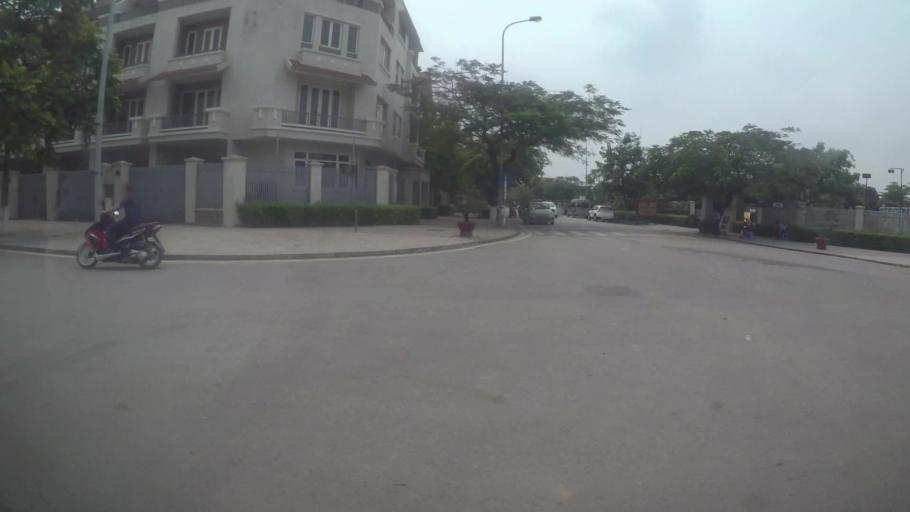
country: VN
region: Ha Noi
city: Ha Dong
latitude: 20.9739
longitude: 105.7539
